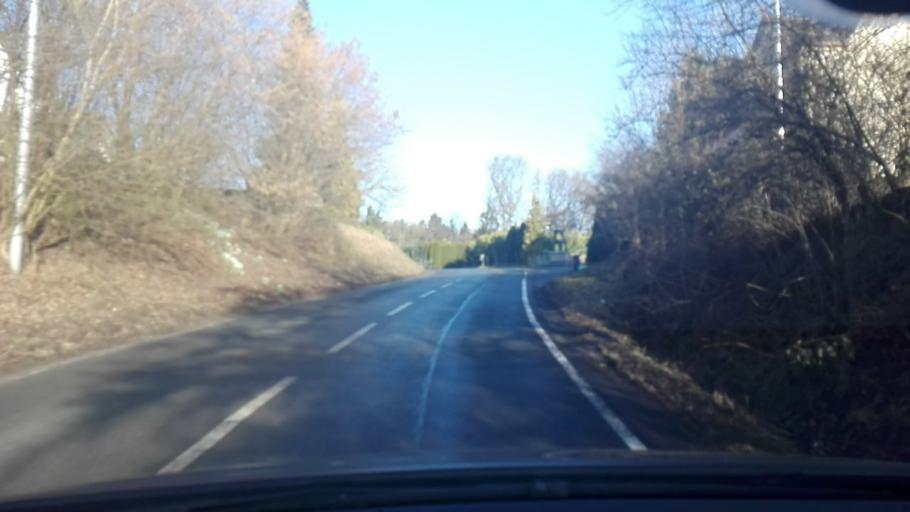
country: DE
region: North Rhine-Westphalia
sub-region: Regierungsbezirk Arnsberg
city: Frondenberg
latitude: 51.4802
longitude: 7.7627
